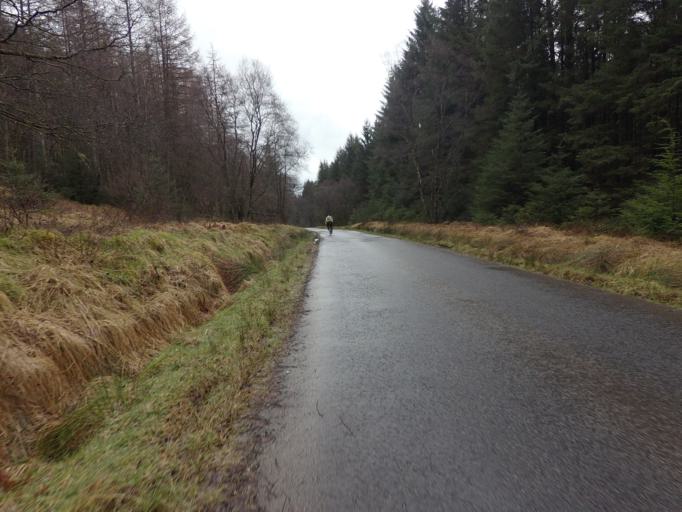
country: GB
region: Scotland
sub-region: West Dunbartonshire
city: Balloch
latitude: 56.2326
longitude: -4.5595
